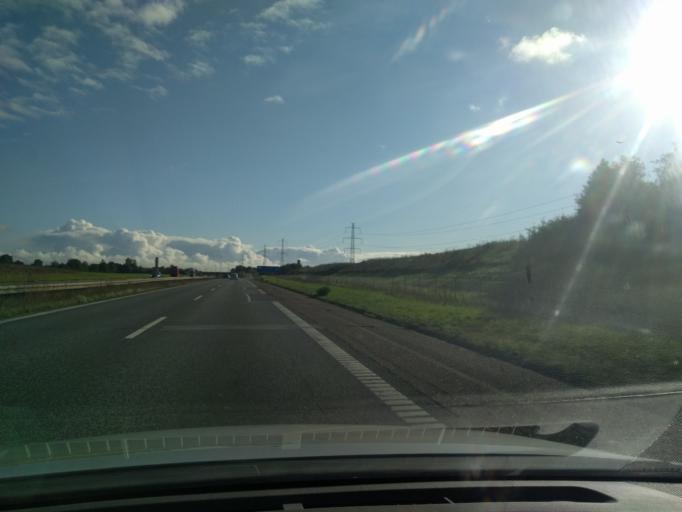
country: DK
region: Zealand
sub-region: Ringsted Kommune
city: Ringsted
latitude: 55.4549
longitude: 11.7770
